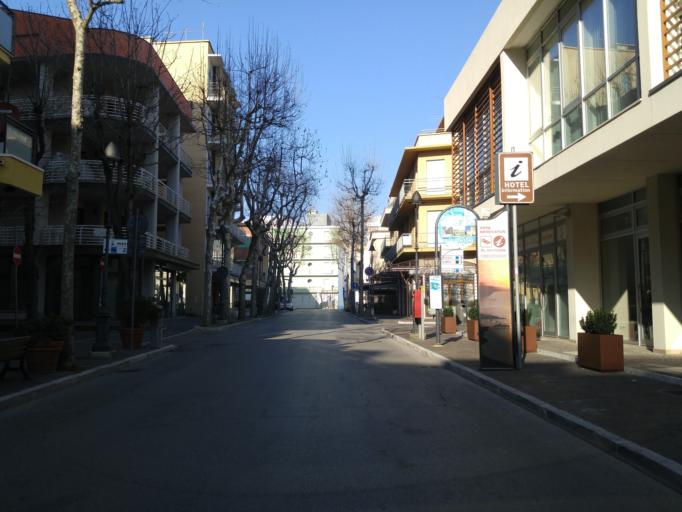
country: IT
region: The Marches
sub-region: Provincia di Pesaro e Urbino
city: Gabicce Mare
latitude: 43.9655
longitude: 12.7565
